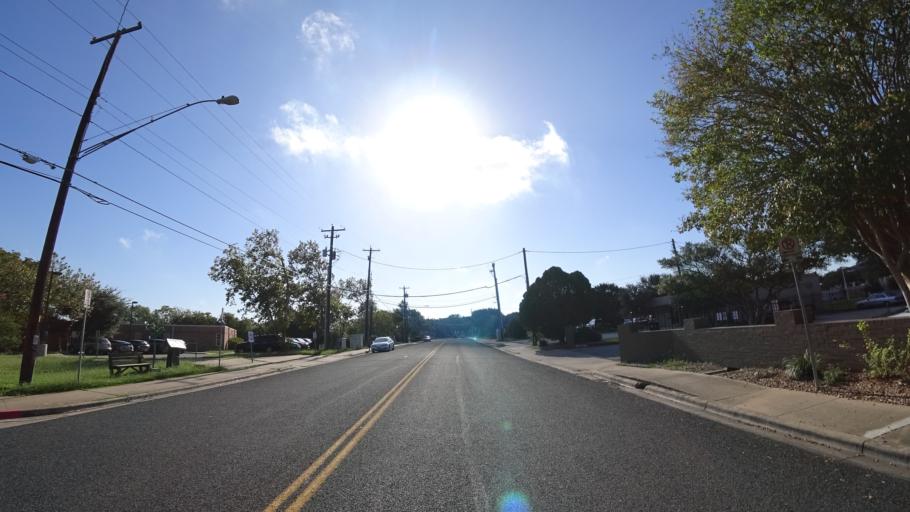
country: US
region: Texas
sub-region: Travis County
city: Rollingwood
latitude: 30.2095
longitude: -97.8064
